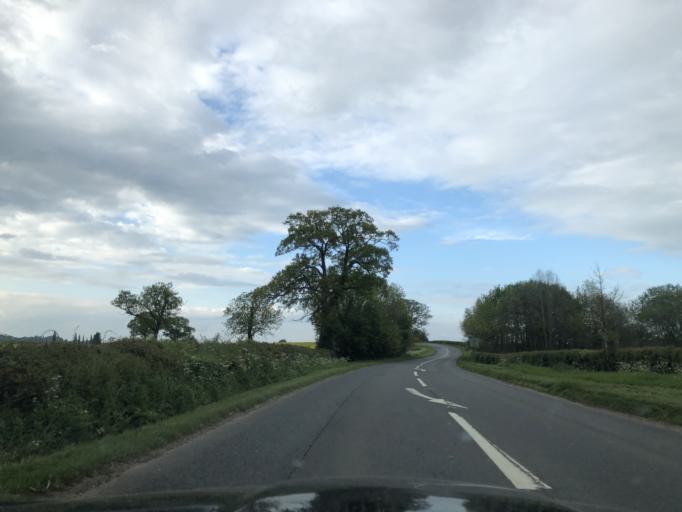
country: GB
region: England
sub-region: Gloucestershire
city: Donnington
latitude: 51.9690
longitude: -1.7095
